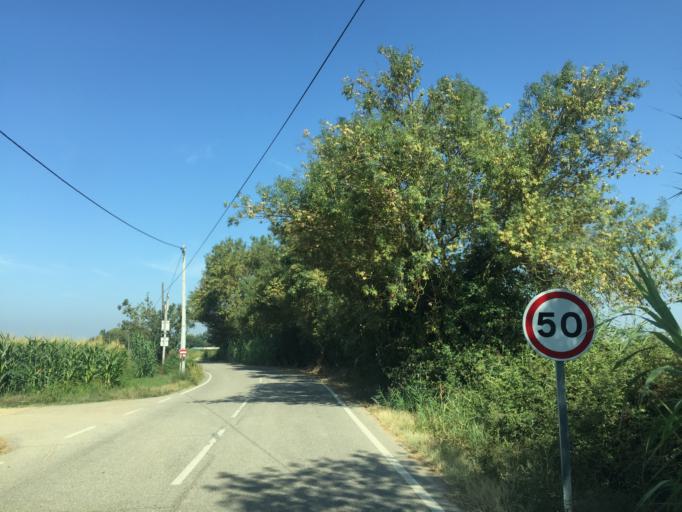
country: PT
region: Santarem
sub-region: Alpiarca
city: Alpiarca
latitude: 39.2941
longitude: -8.5245
